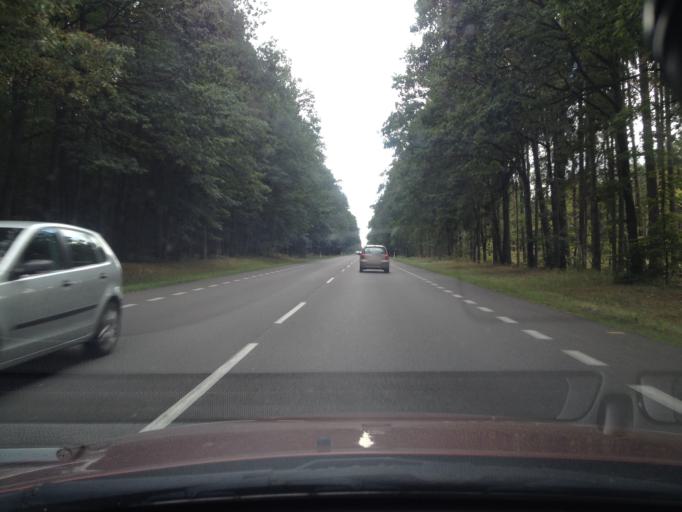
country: PL
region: West Pomeranian Voivodeship
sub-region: Powiat goleniowski
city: Przybiernow
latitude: 53.6732
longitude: 14.8140
